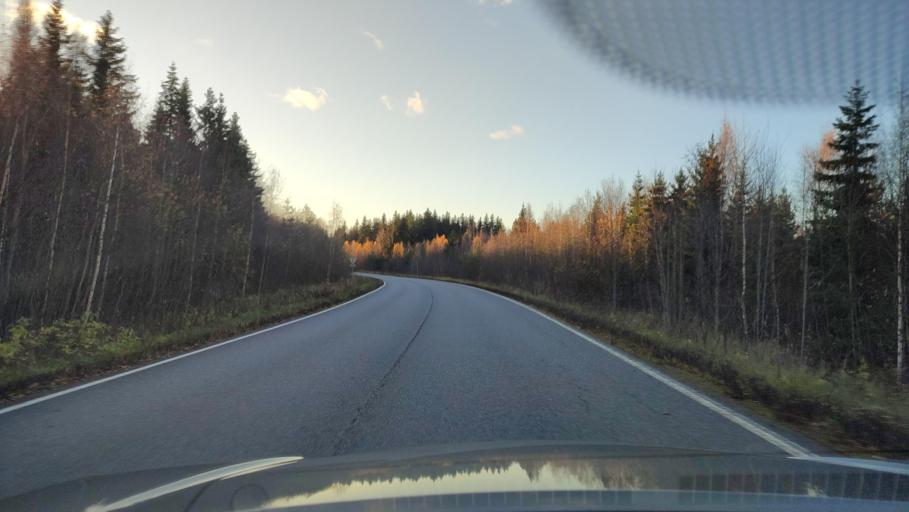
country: FI
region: Ostrobothnia
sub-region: Sydosterbotten
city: Kristinestad
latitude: 62.2960
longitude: 21.3799
